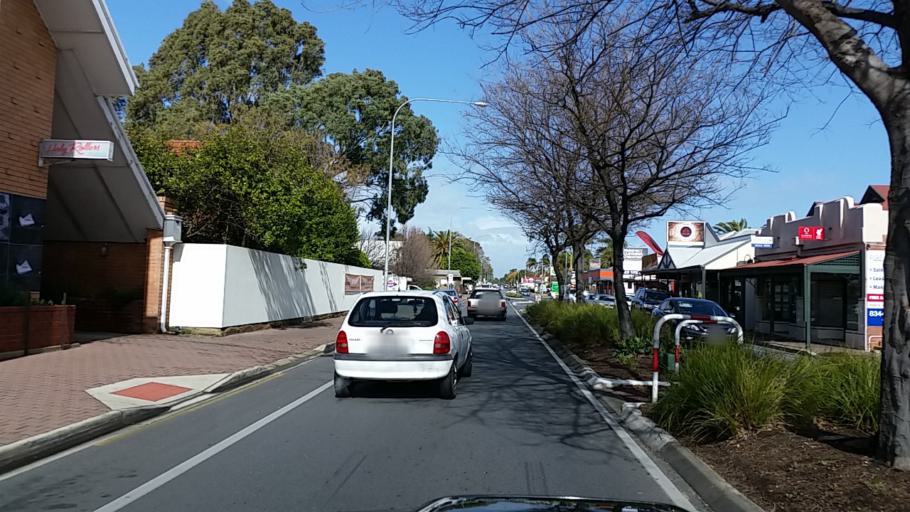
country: AU
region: South Australia
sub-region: Prospect
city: Prospect
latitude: -34.8894
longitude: 138.5942
